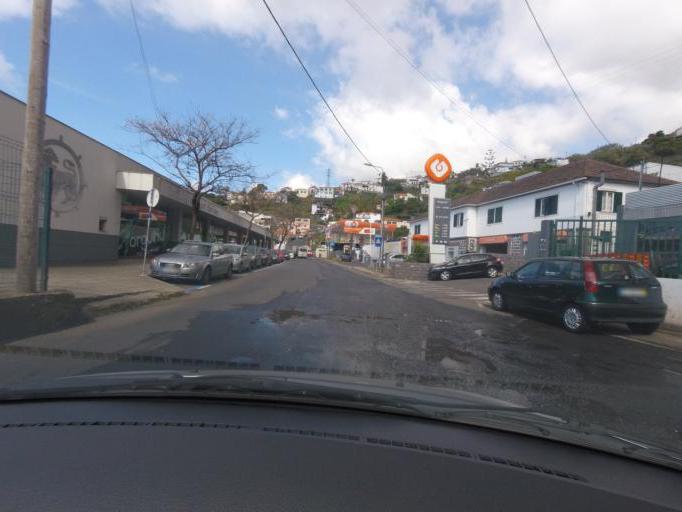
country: PT
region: Madeira
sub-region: Funchal
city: Nossa Senhora do Monte
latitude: 32.6719
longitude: -16.9350
